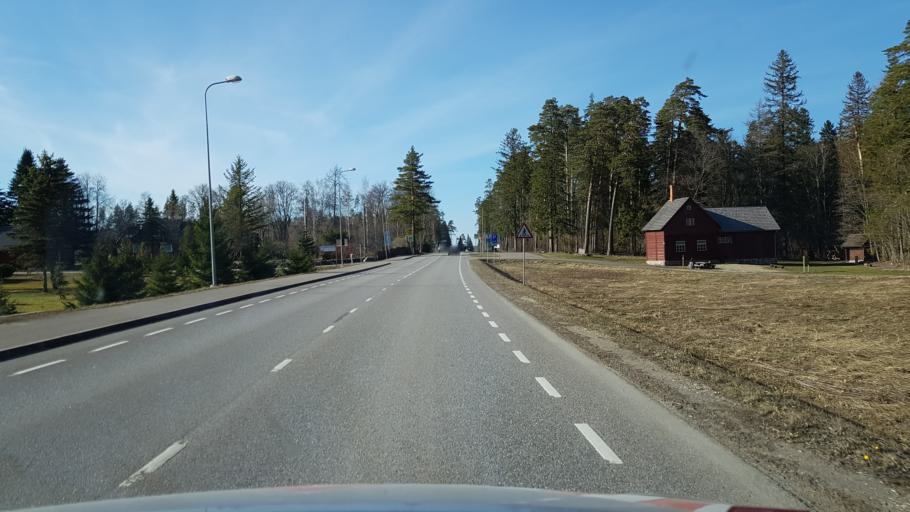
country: EE
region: Laeaene-Virumaa
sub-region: Vinni vald
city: Vinni
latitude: 59.1732
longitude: 26.5809
